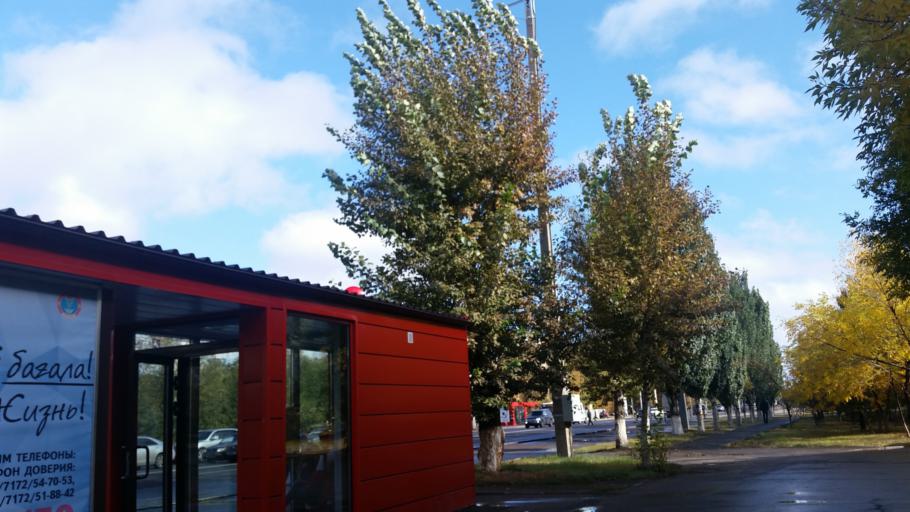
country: KZ
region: Astana Qalasy
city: Astana
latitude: 51.1583
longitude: 71.4754
